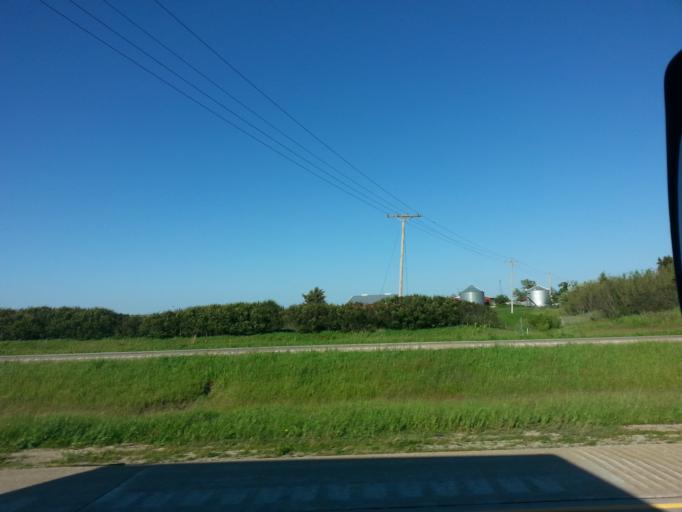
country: US
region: Illinois
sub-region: Woodford County
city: El Paso
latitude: 40.6791
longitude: -89.0282
